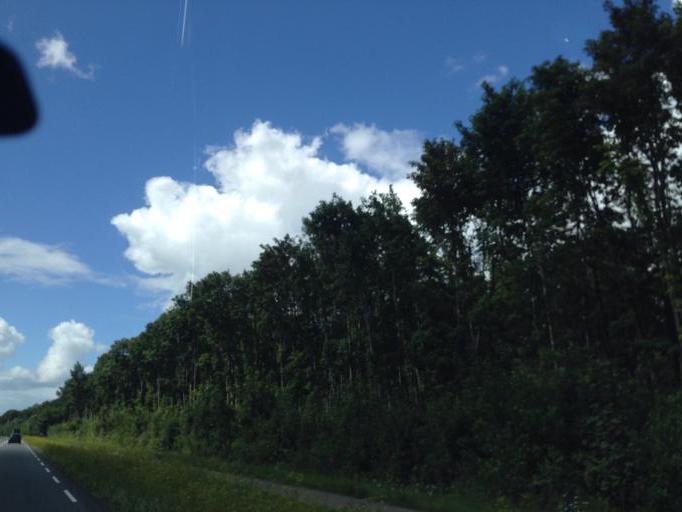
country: NL
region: Overijssel
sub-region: Gemeente Kampen
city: Kampen
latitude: 52.5454
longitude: 5.8340
